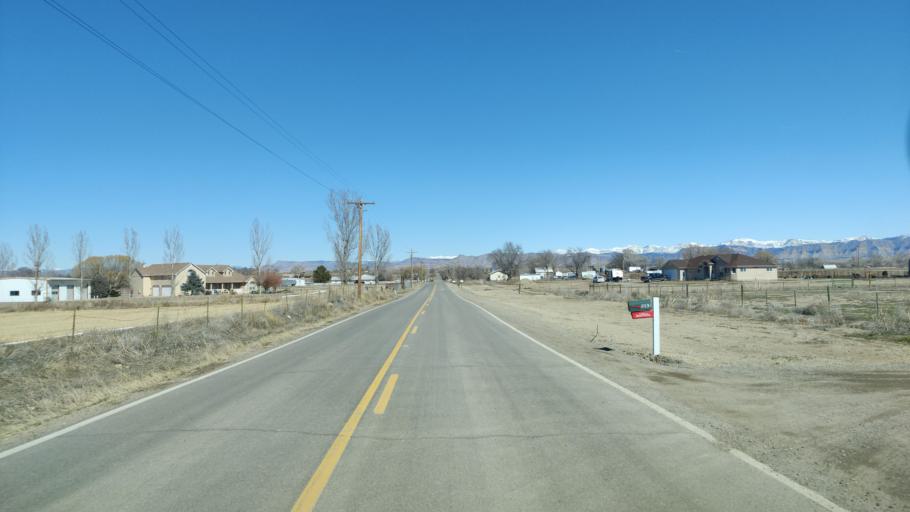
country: US
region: Colorado
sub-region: Mesa County
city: Fruita
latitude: 39.1904
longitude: -108.7105
